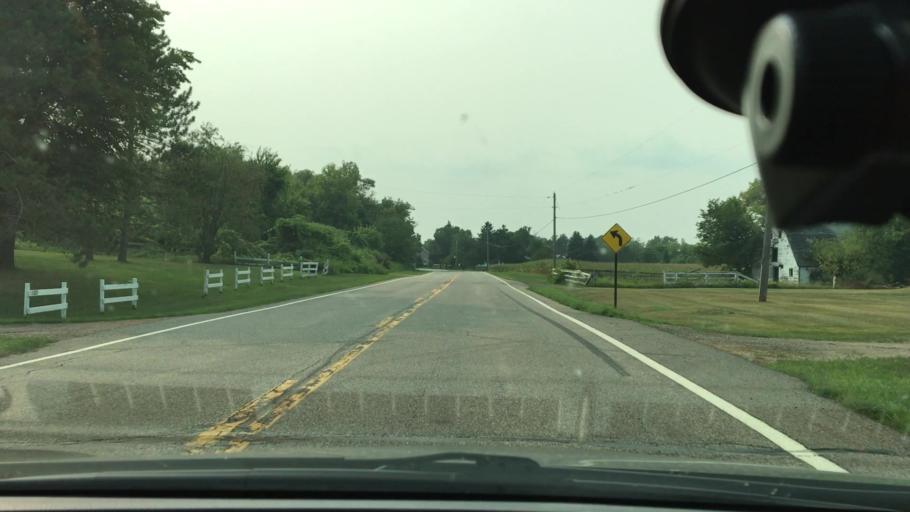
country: US
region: Minnesota
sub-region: Anoka County
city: Ramsey
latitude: 45.2230
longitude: -93.4671
